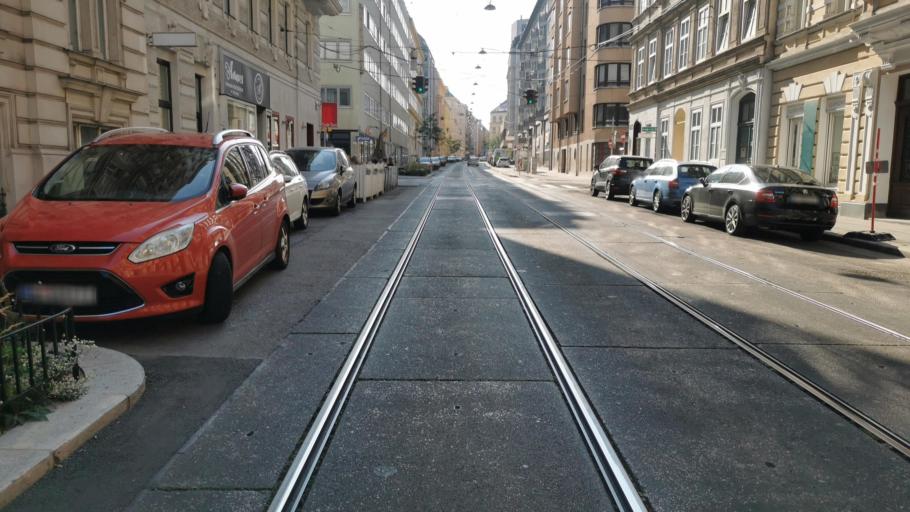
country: AT
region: Vienna
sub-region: Wien Stadt
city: Vienna
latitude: 48.2135
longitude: 16.3488
